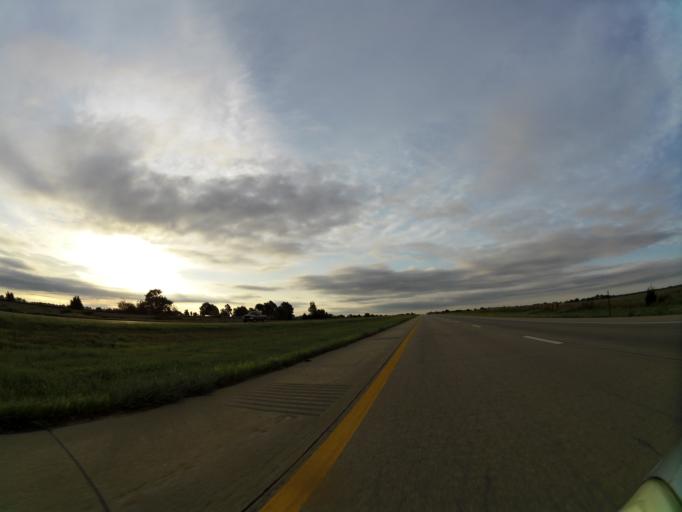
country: US
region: Kansas
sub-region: Reno County
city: Haven
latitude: 37.9271
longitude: -97.8445
